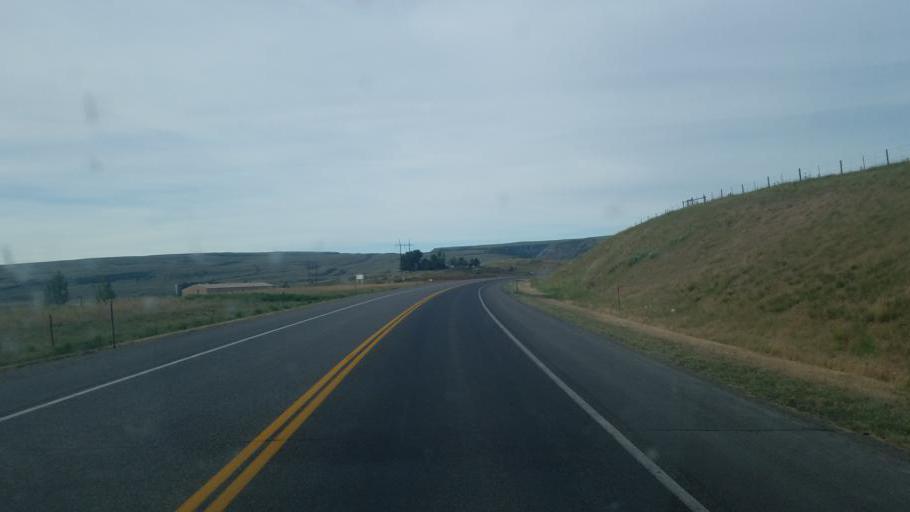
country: US
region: Wyoming
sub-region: Hot Springs County
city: Thermopolis
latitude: 43.6080
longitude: -108.2161
